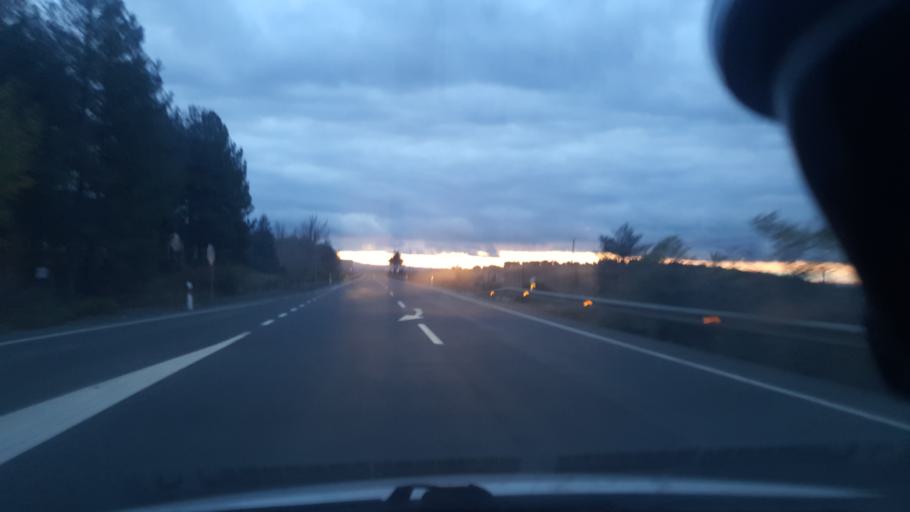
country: ES
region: Castille and Leon
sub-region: Provincia de Avila
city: Ojos-Albos
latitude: 40.7358
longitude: -4.4936
